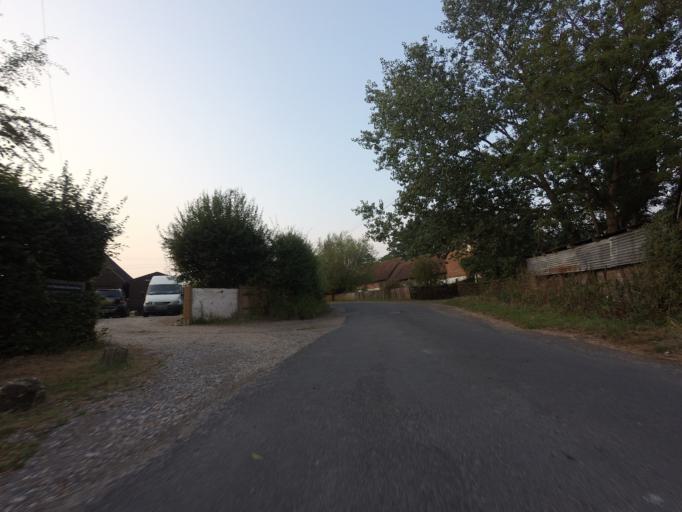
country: GB
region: England
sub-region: Kent
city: Headcorn
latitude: 51.1823
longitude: 0.6695
